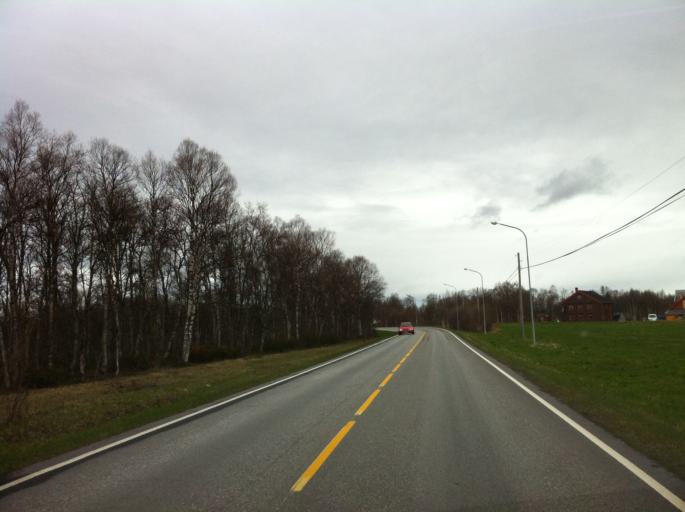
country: NO
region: Sor-Trondelag
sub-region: Tydal
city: Aas
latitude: 62.6428
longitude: 11.8860
